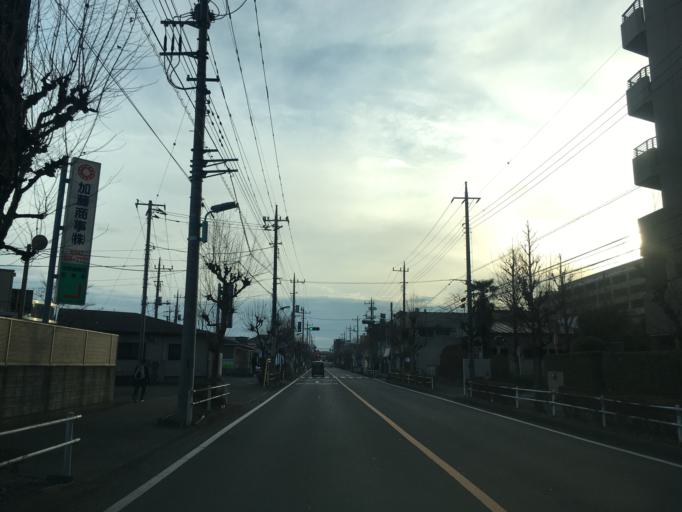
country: JP
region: Saitama
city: Tokorozawa
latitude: 35.8011
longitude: 139.4567
